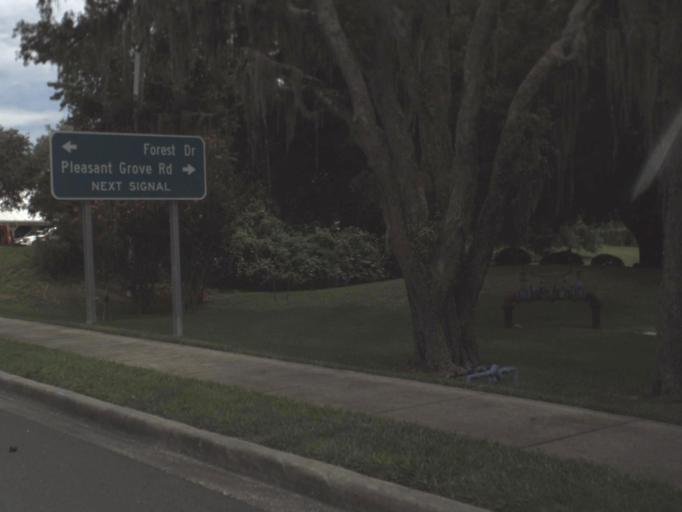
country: US
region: Florida
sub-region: Citrus County
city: Inverness
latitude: 28.8385
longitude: -82.3572
